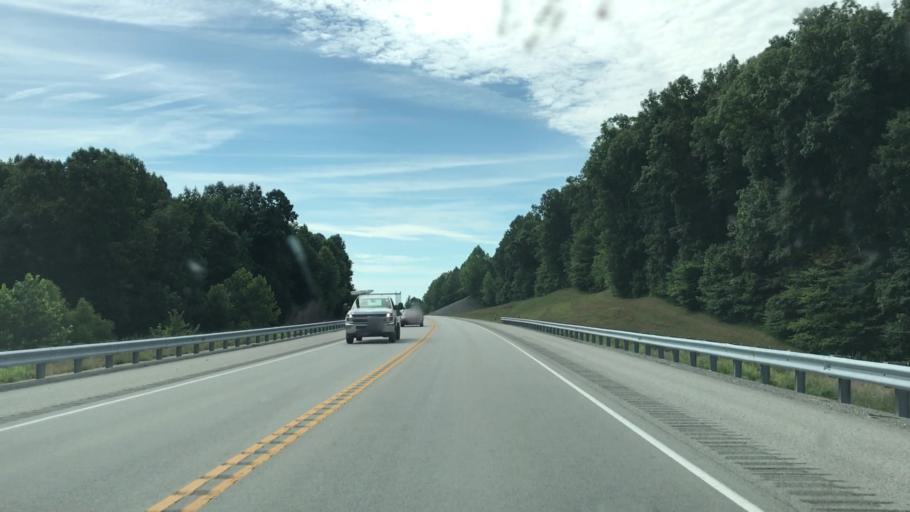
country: US
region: Kentucky
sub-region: Edmonson County
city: Brownsville
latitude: 37.1801
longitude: -86.2442
